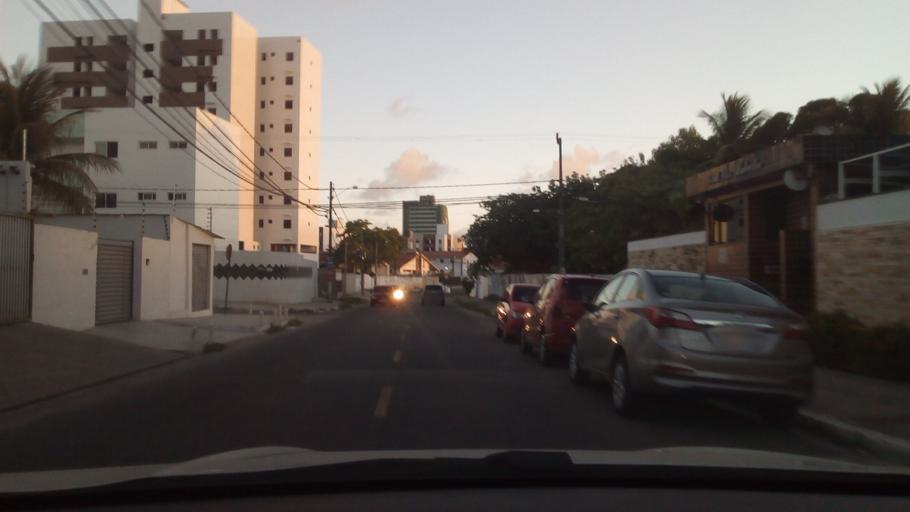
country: BR
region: Paraiba
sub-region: Joao Pessoa
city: Joao Pessoa
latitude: -7.1518
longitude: -34.8420
